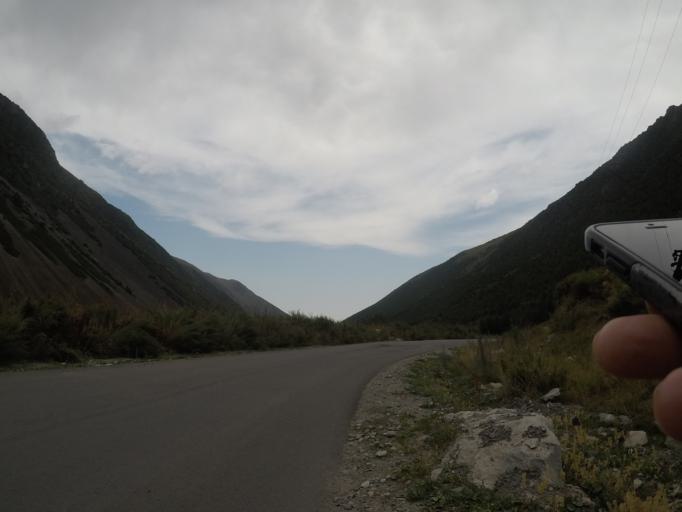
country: KG
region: Chuy
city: Bishkek
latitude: 42.5791
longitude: 74.4816
